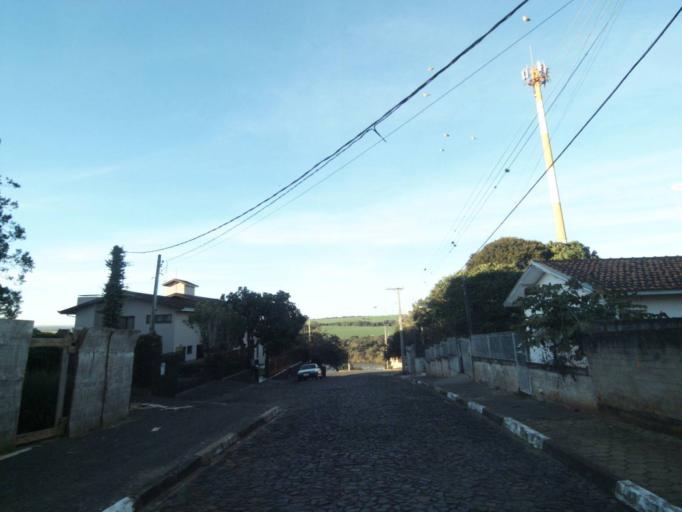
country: BR
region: Parana
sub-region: Tibagi
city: Tibagi
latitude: -24.5157
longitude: -50.4087
